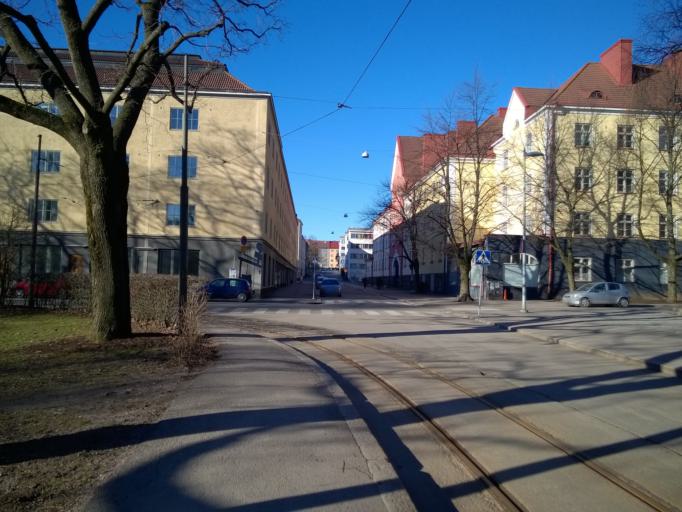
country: FI
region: Uusimaa
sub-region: Helsinki
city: Helsinki
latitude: 60.1972
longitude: 24.9606
